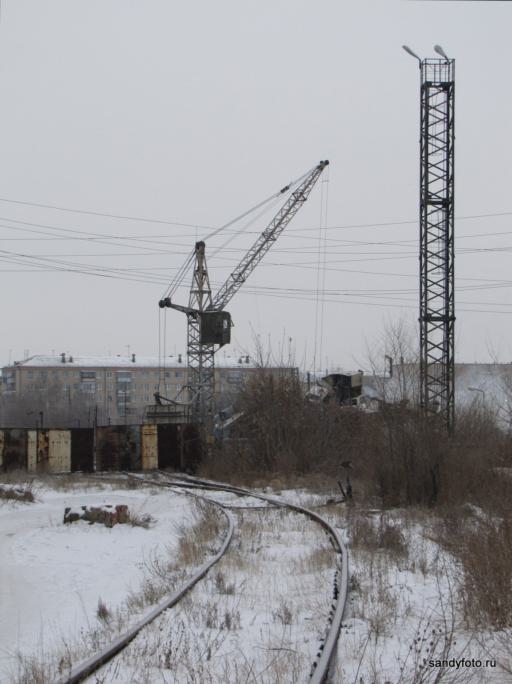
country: RU
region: Chelyabinsk
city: Troitsk
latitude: 54.1041
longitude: 61.5679
